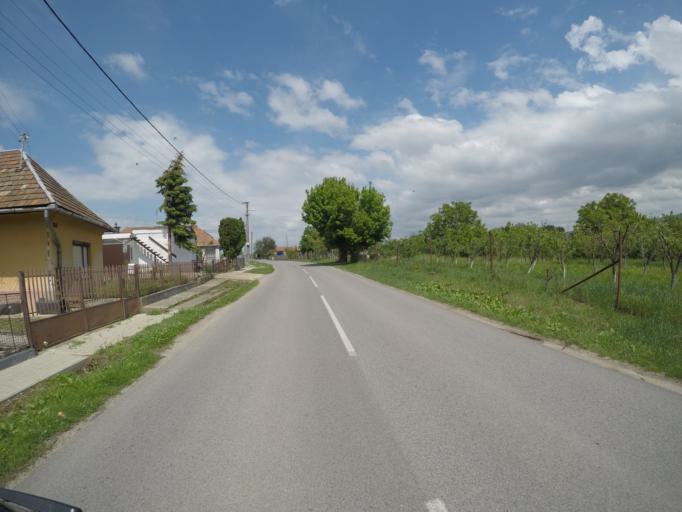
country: SK
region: Nitriansky
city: Zeliezovce
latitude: 47.9747
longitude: 18.7523
